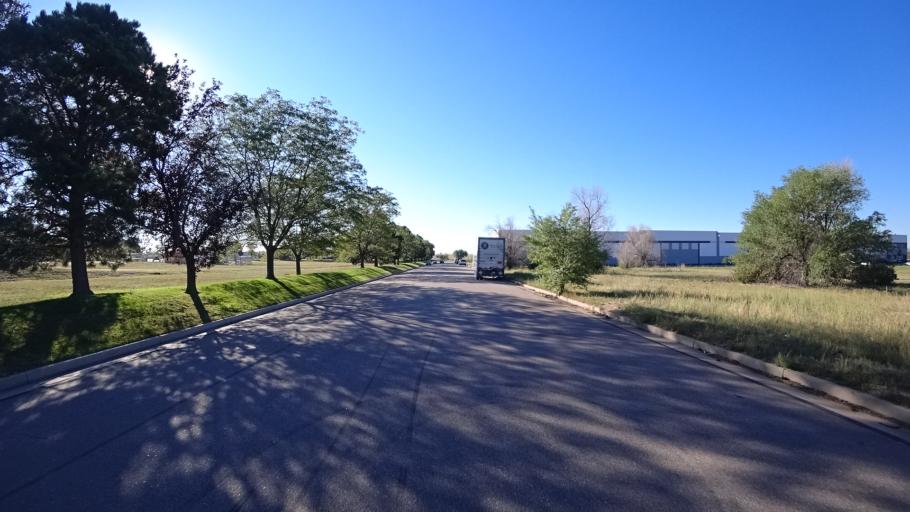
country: US
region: Colorado
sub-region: El Paso County
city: Security-Widefield
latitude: 38.7941
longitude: -104.7269
